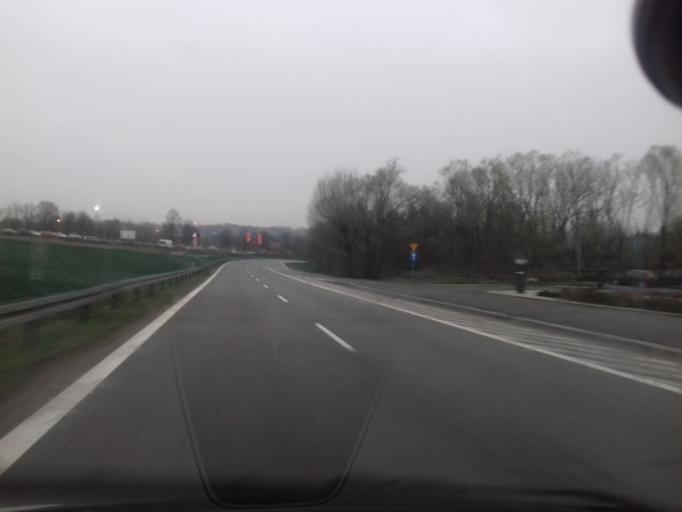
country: PL
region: Lesser Poland Voivodeship
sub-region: Powiat myslenicki
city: Jawornik
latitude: 49.8656
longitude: 19.9103
